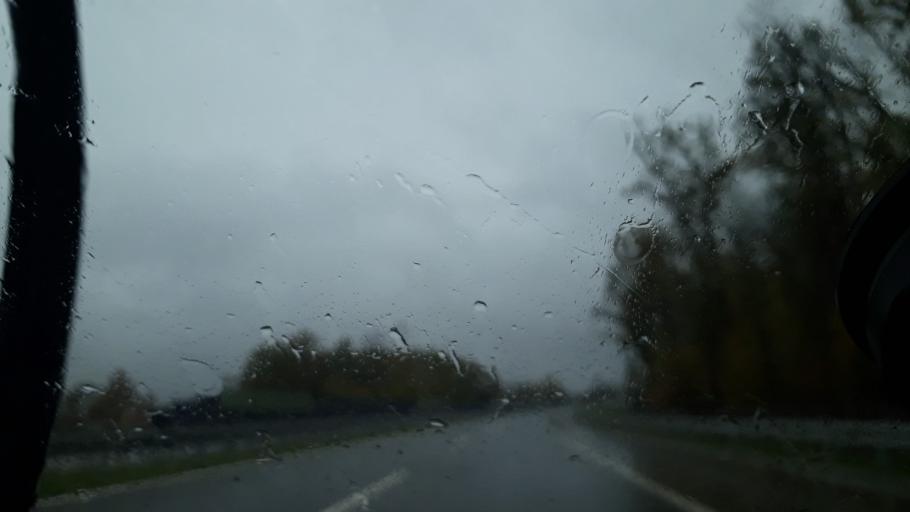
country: BA
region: Republika Srpska
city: Stanari
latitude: 44.8434
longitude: 17.7862
